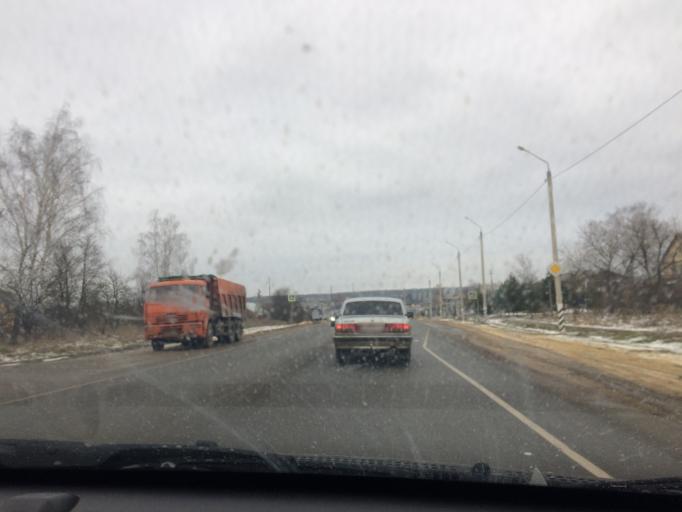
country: RU
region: Tula
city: Gorelki
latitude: 54.2526
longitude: 37.6927
